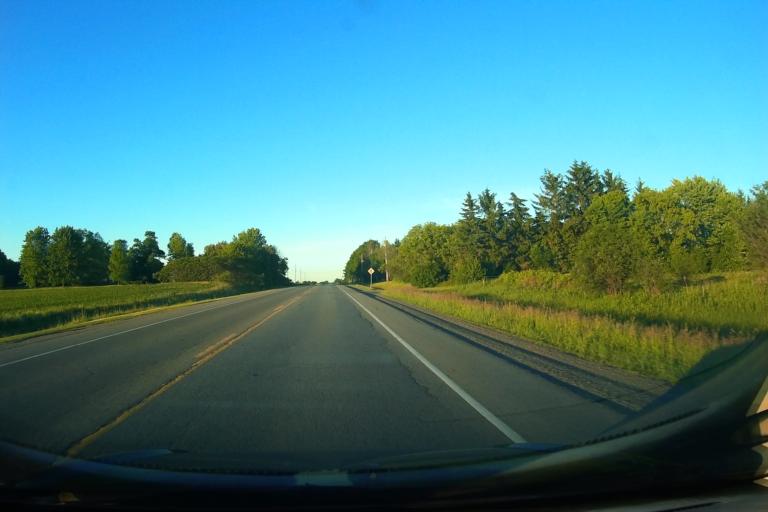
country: CA
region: Ontario
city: Prescott
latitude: 45.0747
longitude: -75.4060
